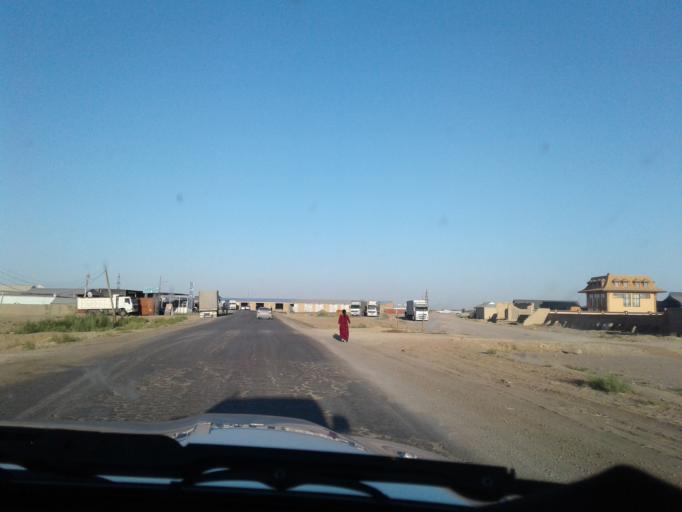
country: TM
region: Mary
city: Mary
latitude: 37.5643
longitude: 61.8209
